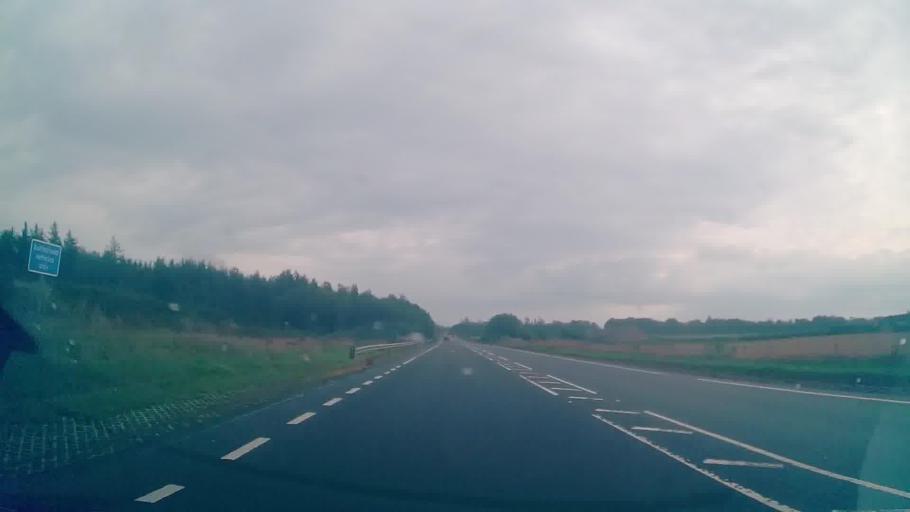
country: GB
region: Scotland
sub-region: Dumfries and Galloway
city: Lockerbie
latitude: 55.0173
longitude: -3.3611
